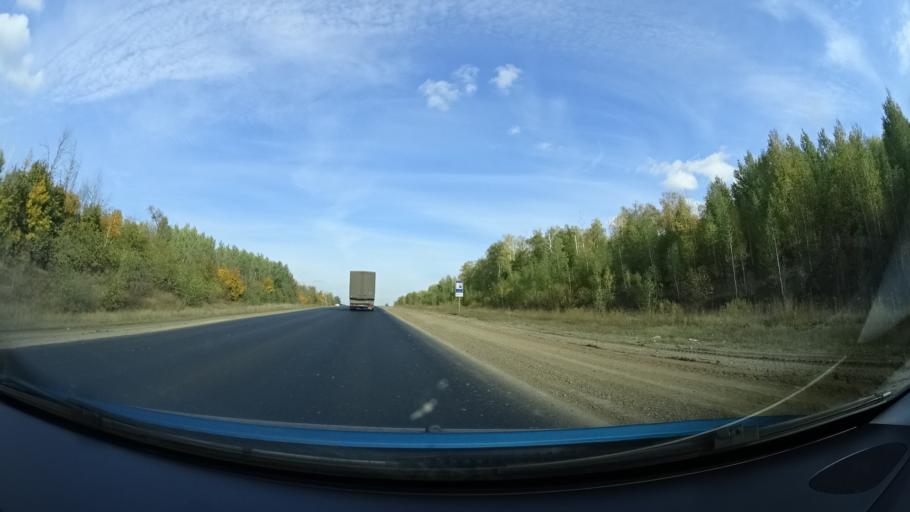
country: RU
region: Bashkortostan
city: Kandry
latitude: 54.5846
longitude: 54.2553
